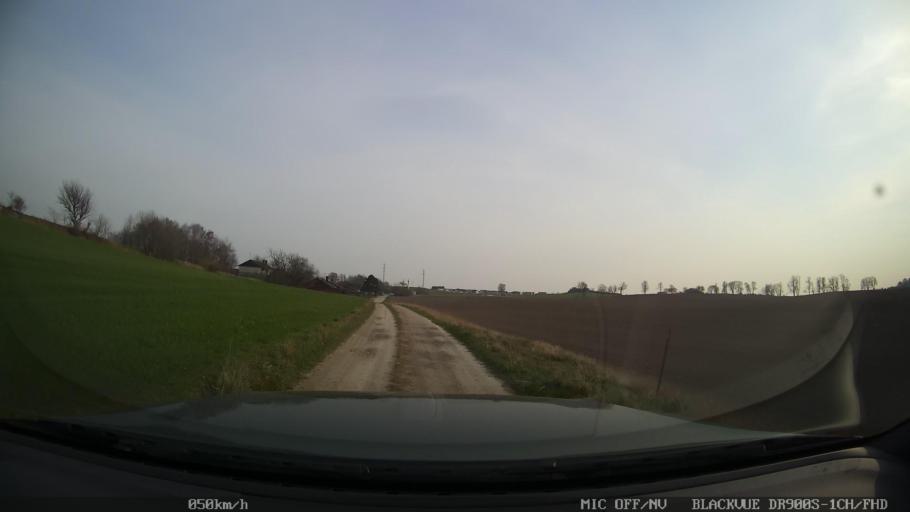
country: SE
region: Skane
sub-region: Ystads Kommun
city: Ystad
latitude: 55.4532
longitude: 13.7935
